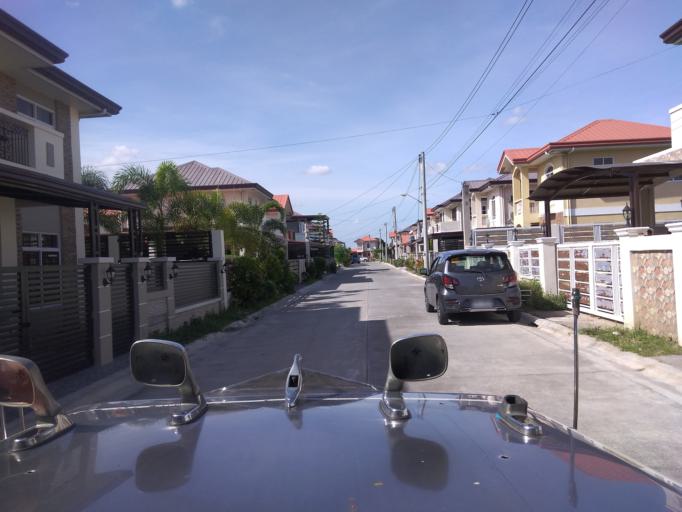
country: PH
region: Central Luzon
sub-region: Province of Pampanga
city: Magliman
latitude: 15.0237
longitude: 120.6604
